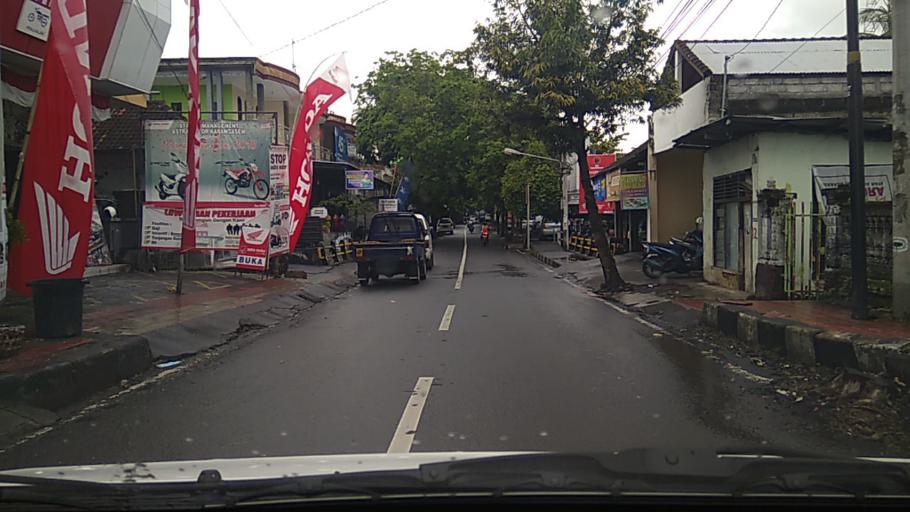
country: ID
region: Bali
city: Karangasem
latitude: -8.4473
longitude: 115.6147
